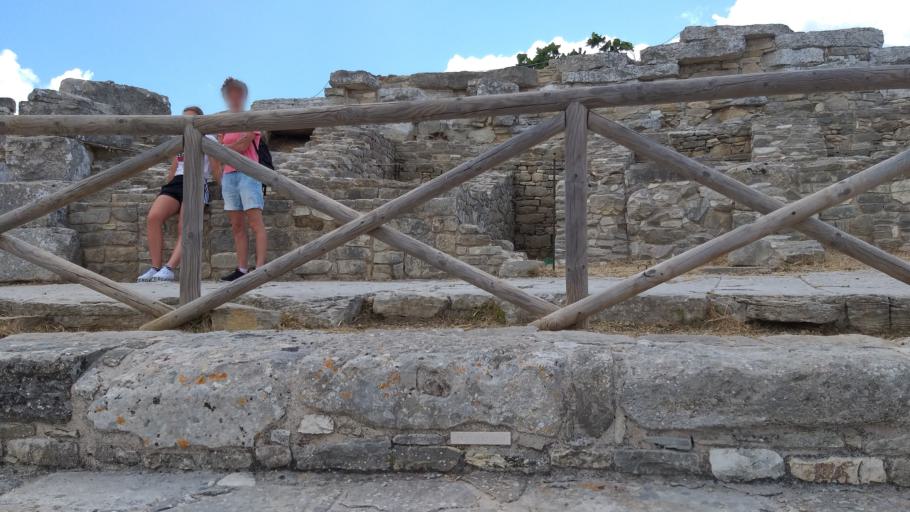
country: IT
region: Sicily
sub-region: Trapani
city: Calatafimi
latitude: 37.9411
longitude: 12.8437
